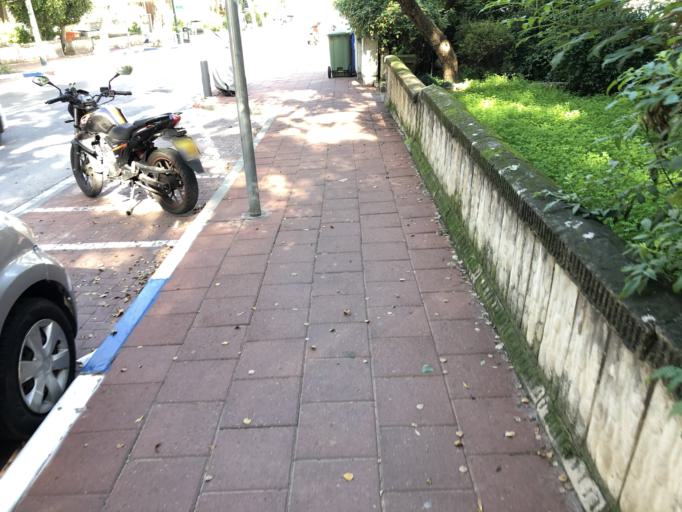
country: IL
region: Tel Aviv
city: Bene Beraq
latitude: 32.0762
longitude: 34.8252
